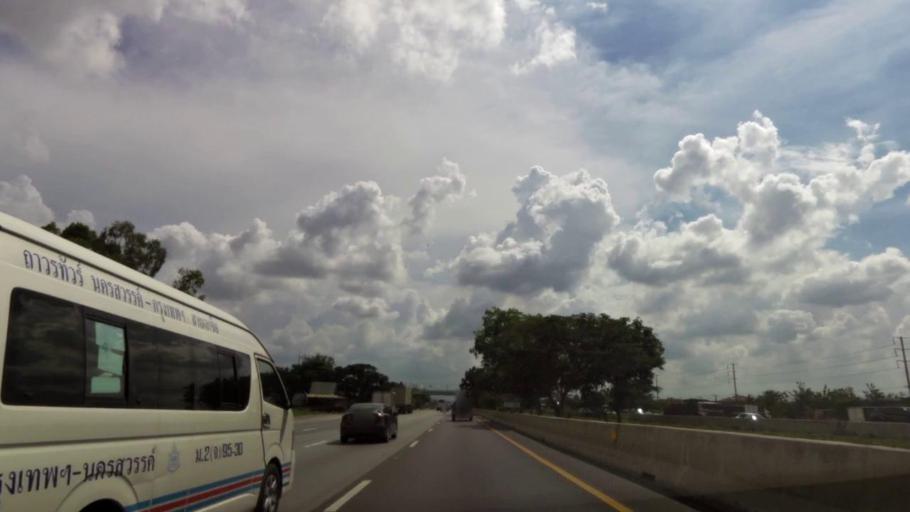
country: TH
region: Phra Nakhon Si Ayutthaya
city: Phra Nakhon Si Ayutthaya
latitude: 14.2902
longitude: 100.6134
